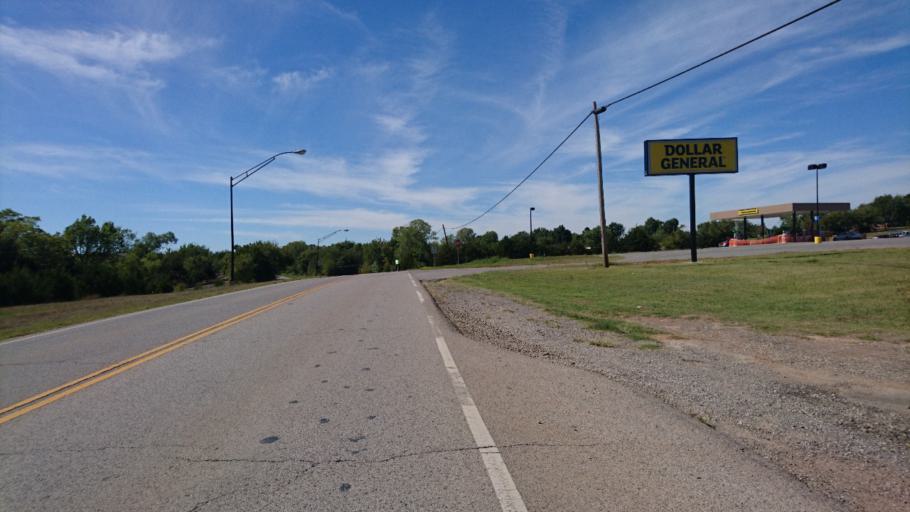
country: US
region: Oklahoma
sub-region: Lincoln County
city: Stroud
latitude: 35.7509
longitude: -96.6715
